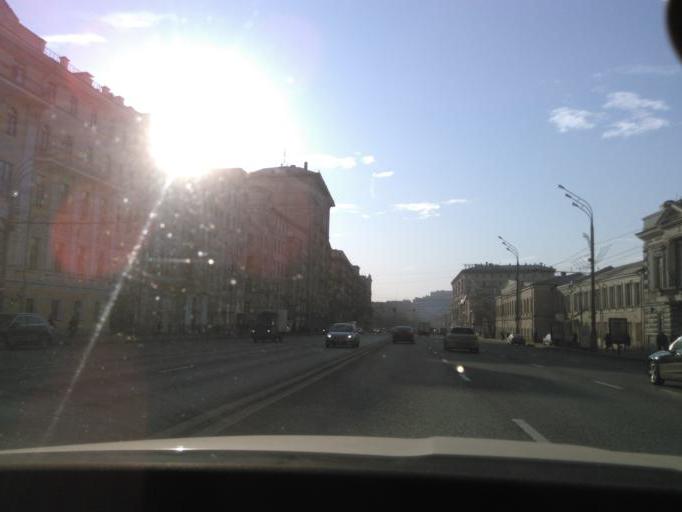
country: RU
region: Moscow
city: Taganskiy
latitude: 55.7676
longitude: 37.6512
